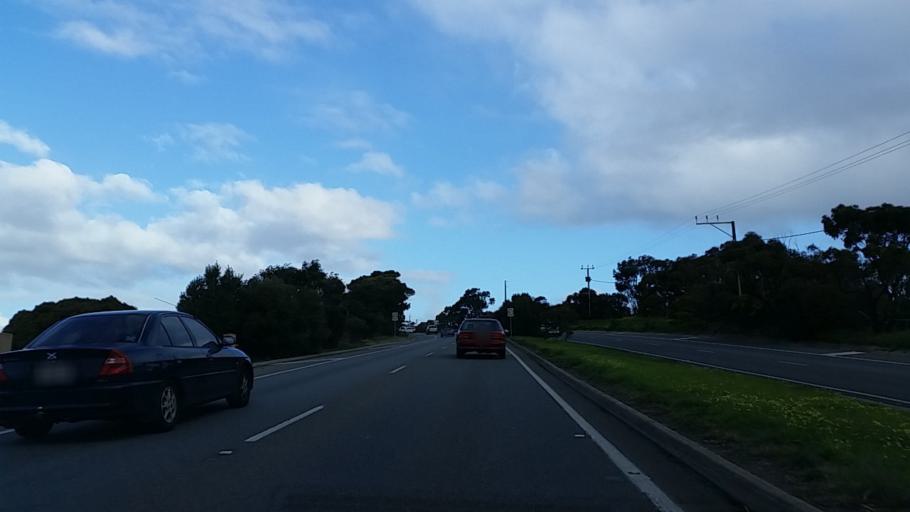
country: AU
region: South Australia
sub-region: Adelaide Hills
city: Seacliff
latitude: -35.0464
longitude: 138.5318
